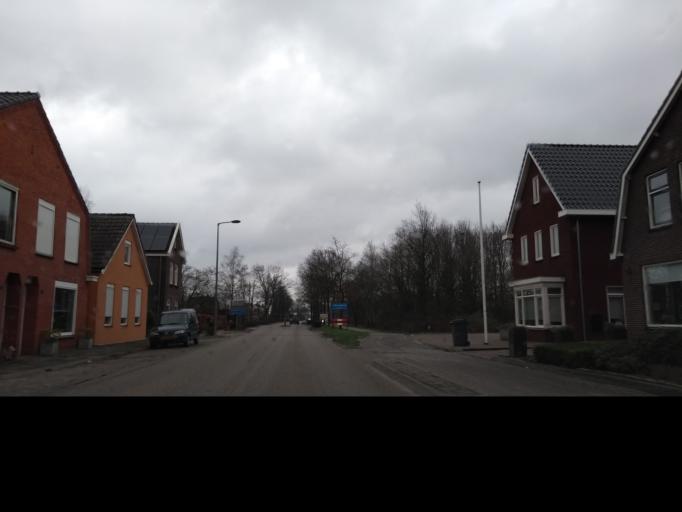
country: NL
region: Overijssel
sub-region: Gemeente Losser
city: Losser
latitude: 52.2234
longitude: 6.9761
